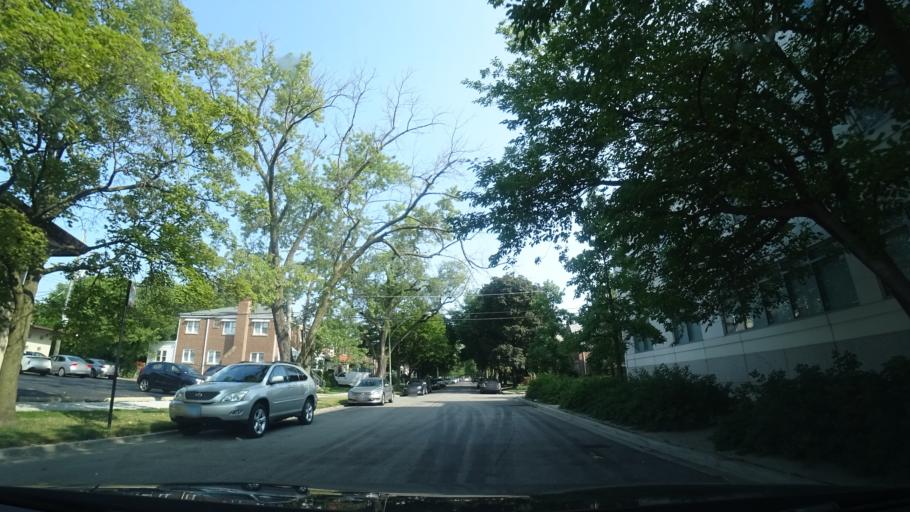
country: US
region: Illinois
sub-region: Cook County
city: Lincolnwood
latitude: 41.9904
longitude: -87.7128
